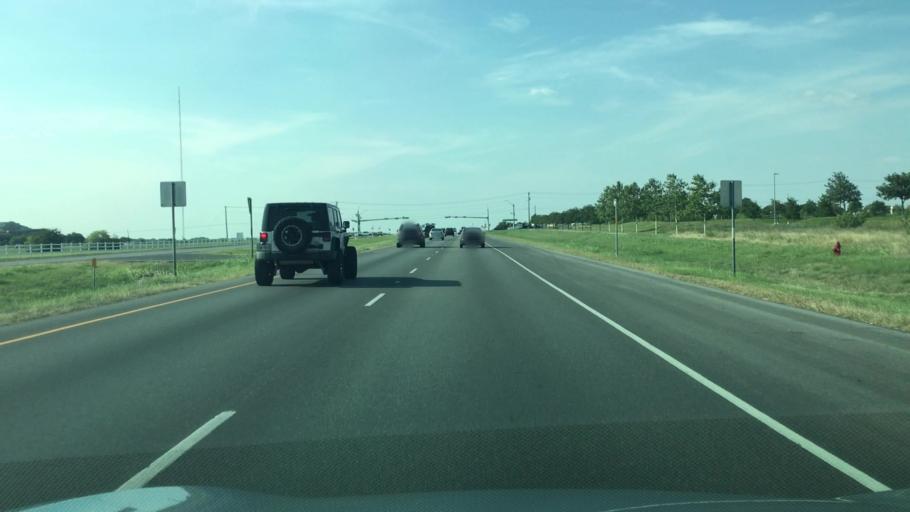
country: US
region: Texas
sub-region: Hays County
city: Kyle
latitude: 30.0251
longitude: -97.8723
